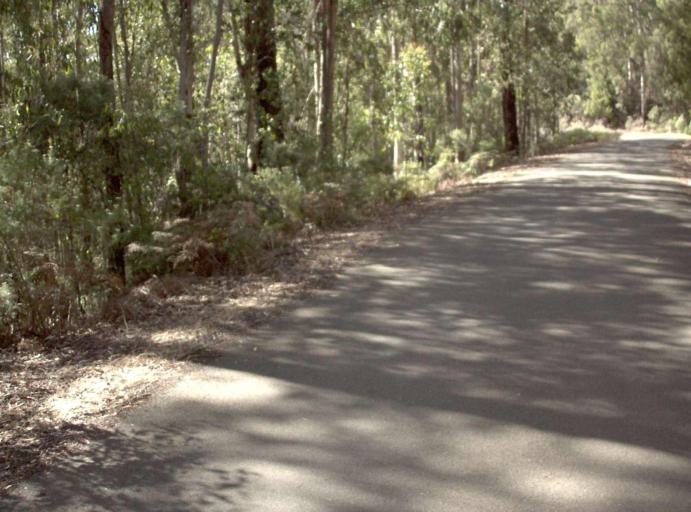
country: AU
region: Victoria
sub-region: East Gippsland
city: Lakes Entrance
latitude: -37.4143
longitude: 148.1202
